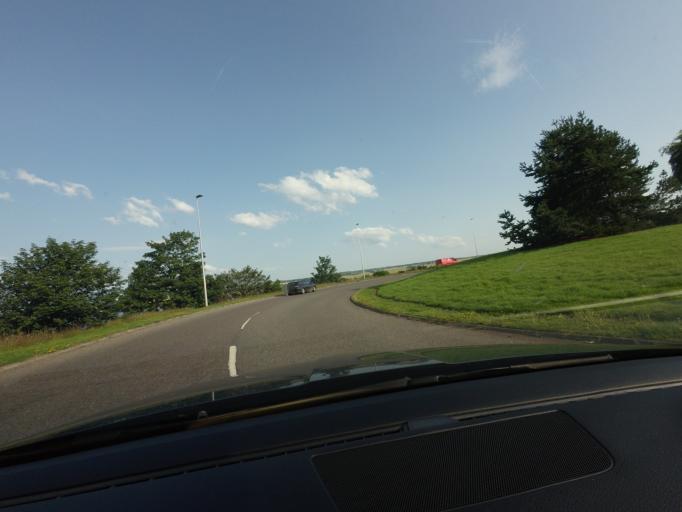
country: GB
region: Scotland
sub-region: Highland
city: Evanton
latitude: 57.6283
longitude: -4.3670
